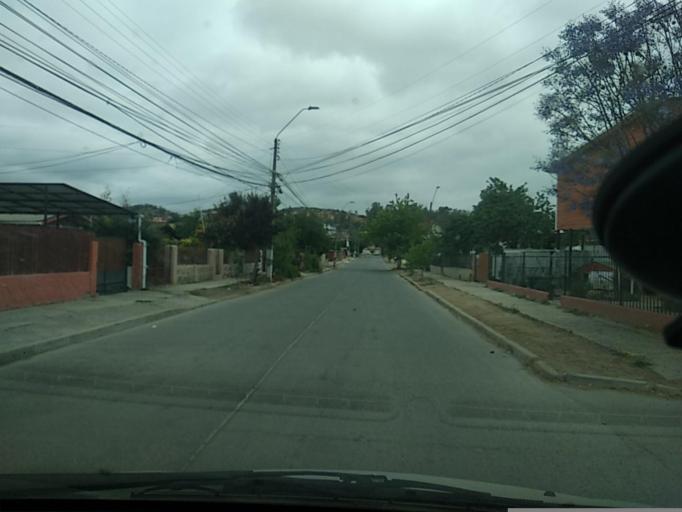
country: CL
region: Valparaiso
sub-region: Provincia de Marga Marga
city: Villa Alemana
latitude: -33.0399
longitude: -71.3618
